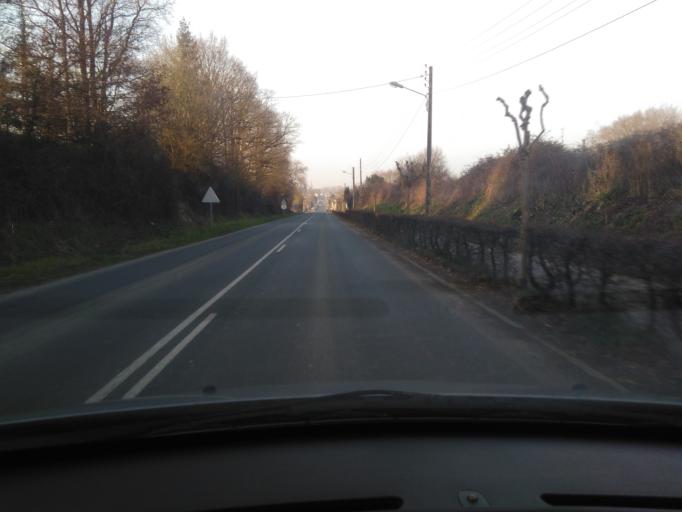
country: FR
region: Pays de la Loire
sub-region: Departement de la Vendee
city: Chantonnay
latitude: 46.6722
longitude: -1.0487
